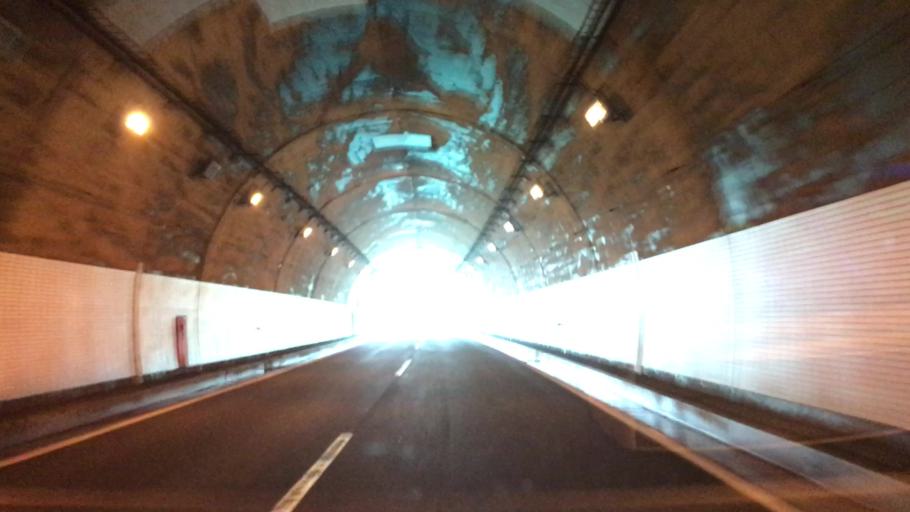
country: JP
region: Hokkaido
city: Shiraoi
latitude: 42.4746
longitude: 141.2161
